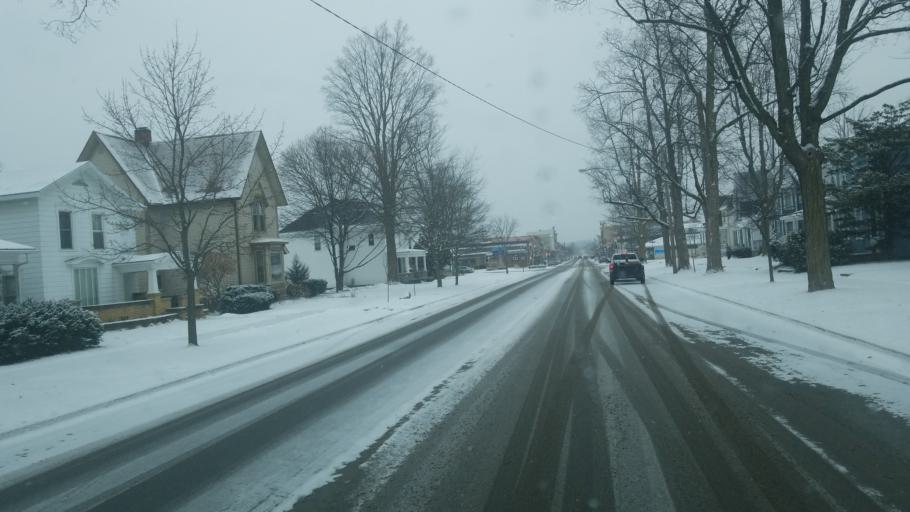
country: US
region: Michigan
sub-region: Mecosta County
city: Big Rapids
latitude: 43.6945
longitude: -85.4819
